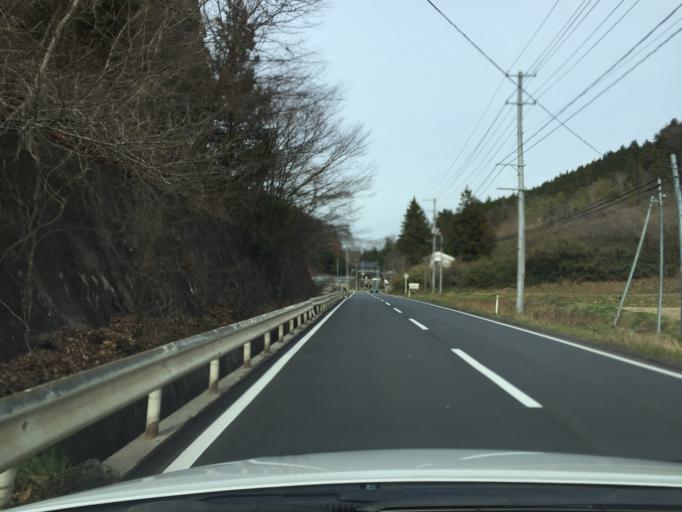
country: JP
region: Fukushima
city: Ishikawa
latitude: 37.2356
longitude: 140.6285
